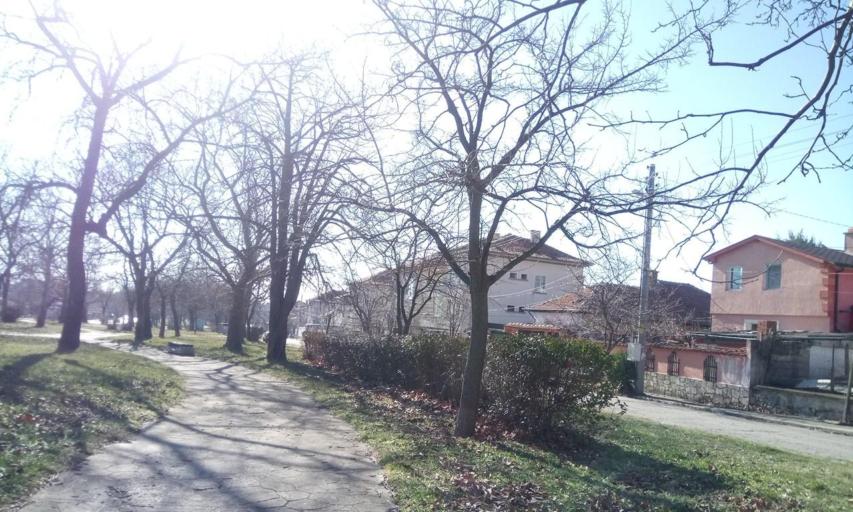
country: BG
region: Plovdiv
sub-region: Obshtina Khisarya
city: Khisarya
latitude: 42.5122
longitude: 24.7159
